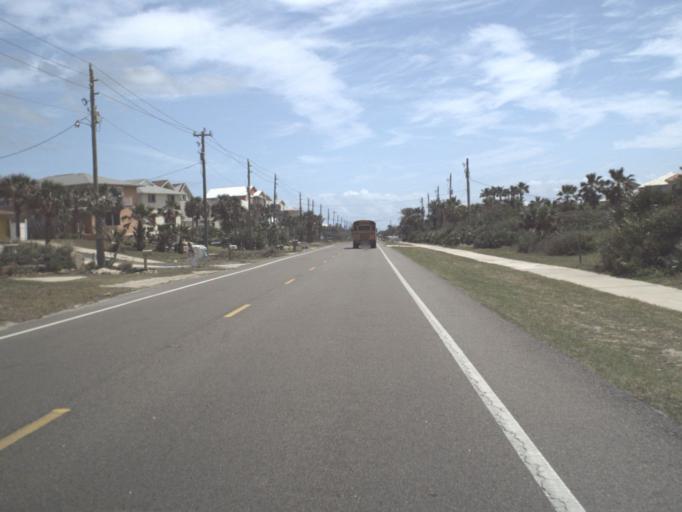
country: US
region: Florida
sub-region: Flagler County
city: Palm Coast
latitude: 29.5421
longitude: -81.1582
